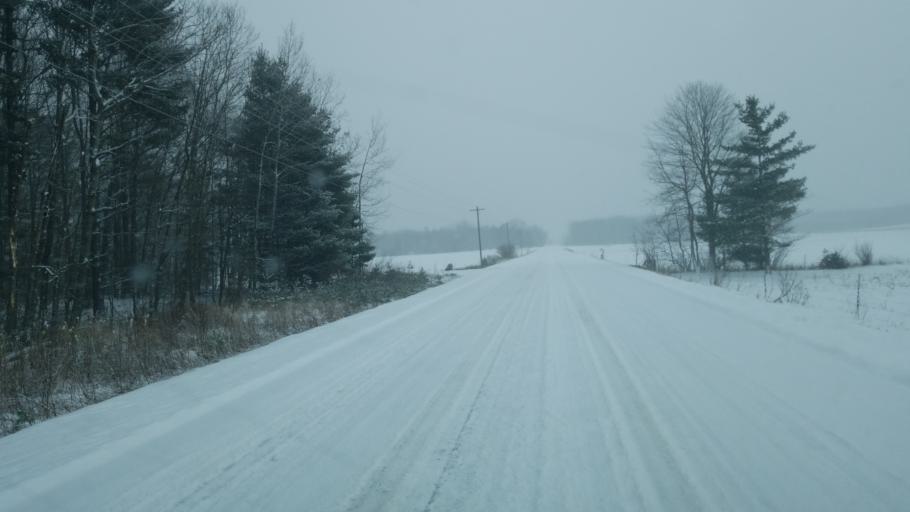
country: US
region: Michigan
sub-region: Mecosta County
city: Canadian Lakes
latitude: 43.5761
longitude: -85.3498
